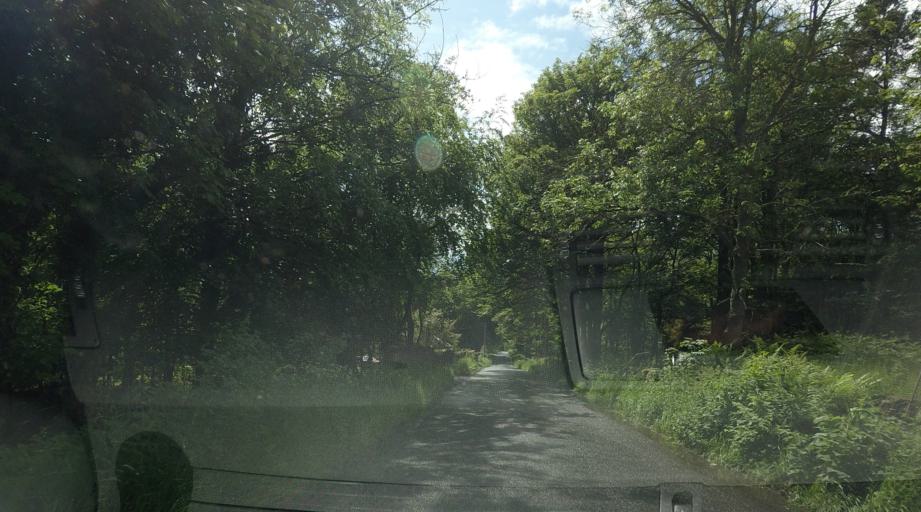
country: GB
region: Scotland
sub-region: Fife
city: Ballingry
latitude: 56.1566
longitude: -3.3602
